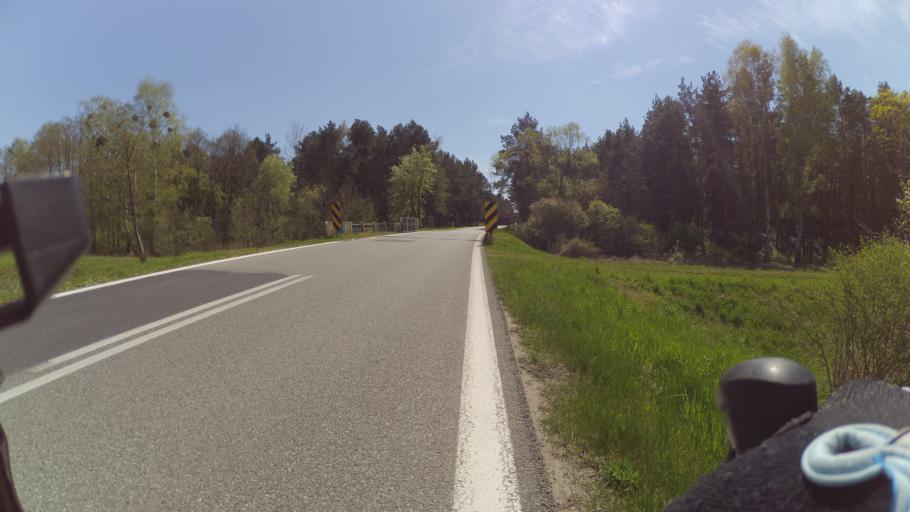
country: PL
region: Masovian Voivodeship
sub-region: Powiat plonski
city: Czerwinsk Nad Wisla
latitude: 52.3693
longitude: 20.3084
